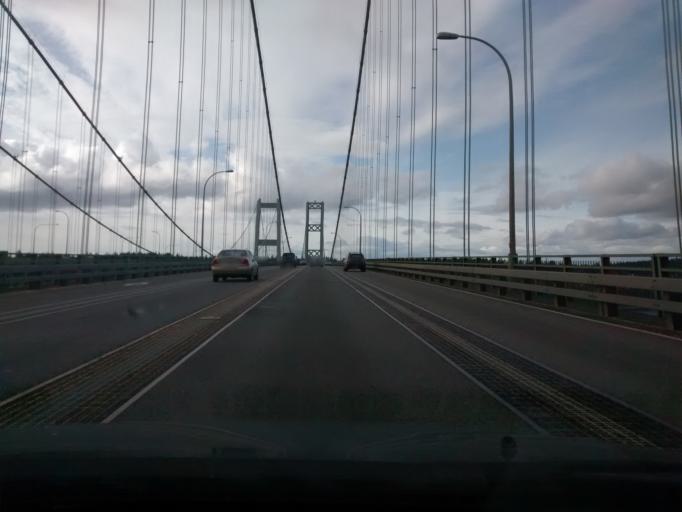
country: US
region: Washington
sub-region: Pierce County
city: University Place
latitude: 47.2658
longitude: -122.5471
